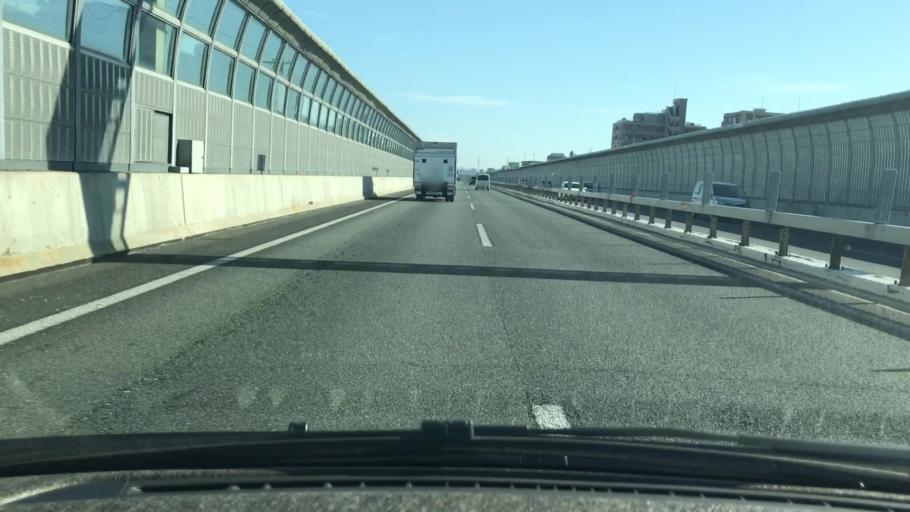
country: JP
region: Hyogo
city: Amagasaki
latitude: 34.7435
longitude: 135.3918
